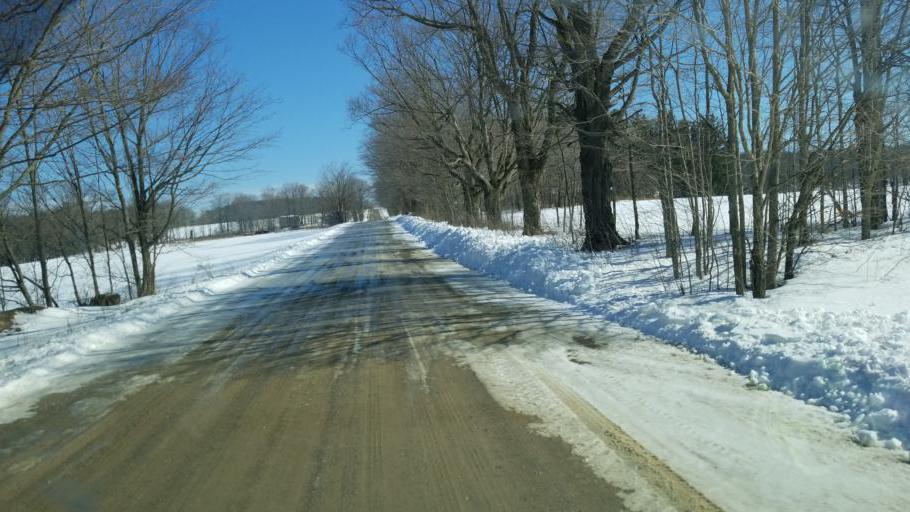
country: US
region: New York
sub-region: Allegany County
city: Andover
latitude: 42.1691
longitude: -77.7243
